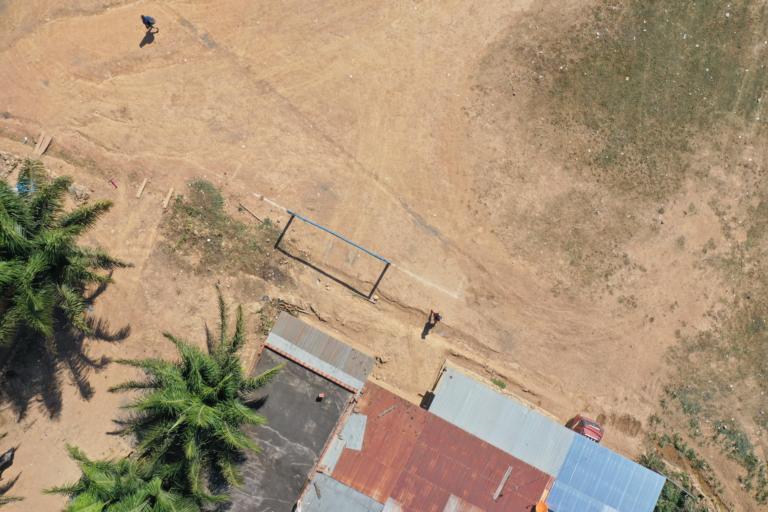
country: BO
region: La Paz
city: Mapiri
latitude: -15.3050
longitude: -68.2133
